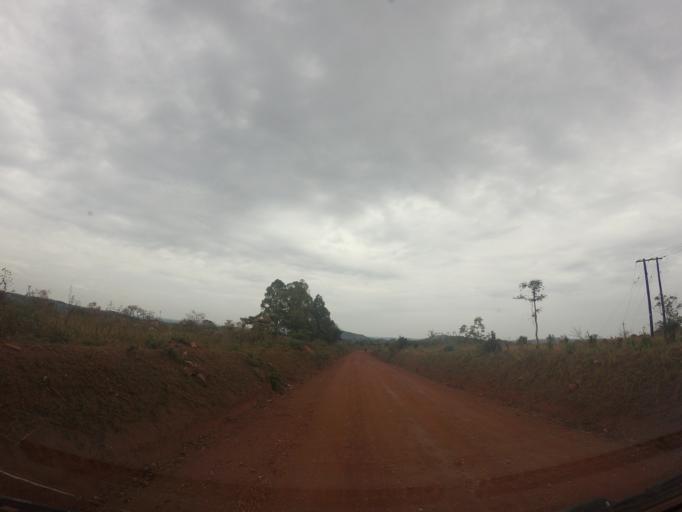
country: UG
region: Northern Region
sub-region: Arua District
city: Arua
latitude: 2.7763
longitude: 30.8614
